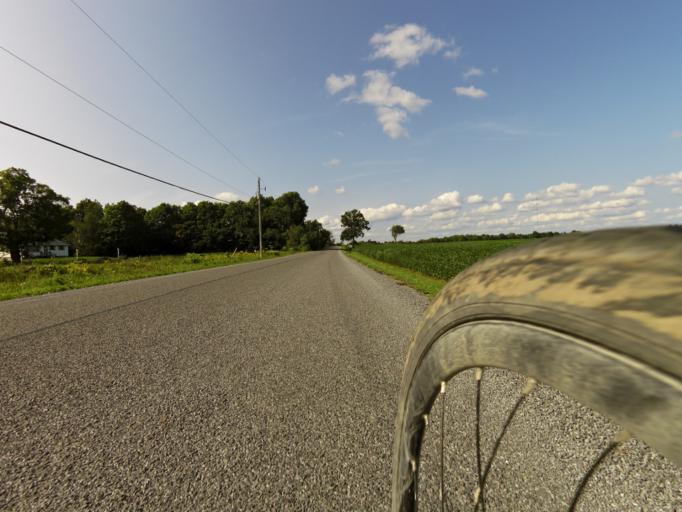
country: CA
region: Ontario
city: Kingston
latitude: 44.3902
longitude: -76.5960
